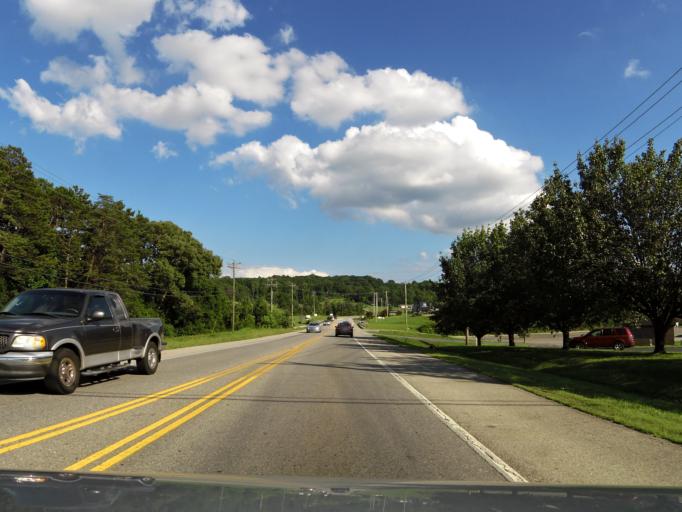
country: US
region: Tennessee
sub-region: Blount County
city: Maryville
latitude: 35.7288
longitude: -84.0313
